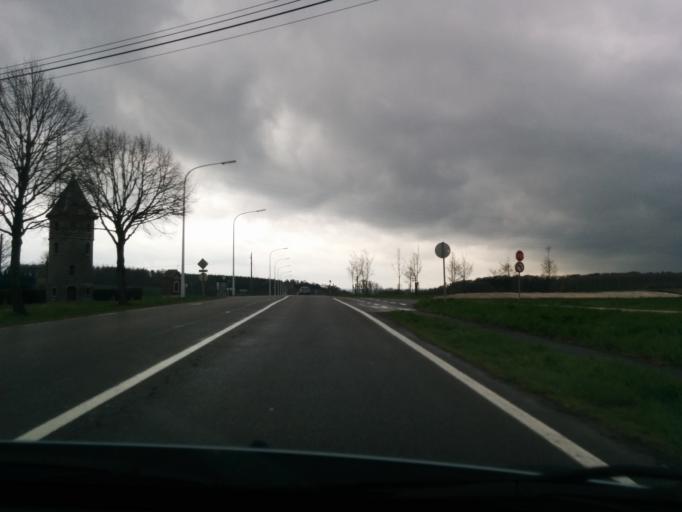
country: BE
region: Wallonia
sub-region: Province de Namur
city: Floreffe
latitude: 50.4748
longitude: 4.7786
